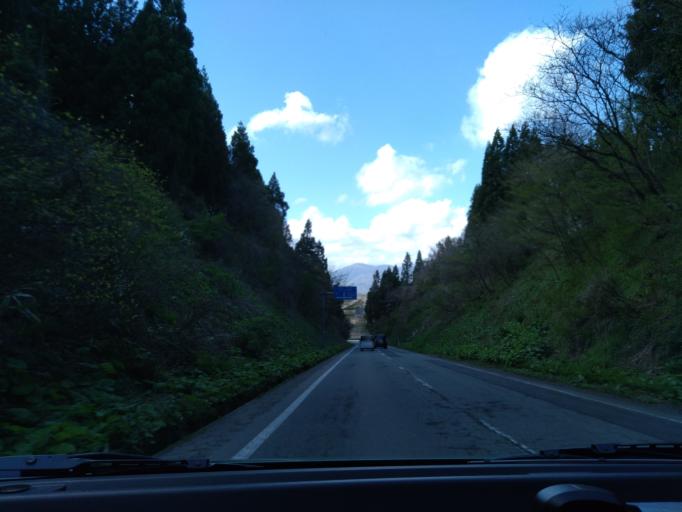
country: JP
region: Akita
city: Akita
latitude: 39.6908
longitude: 140.2747
